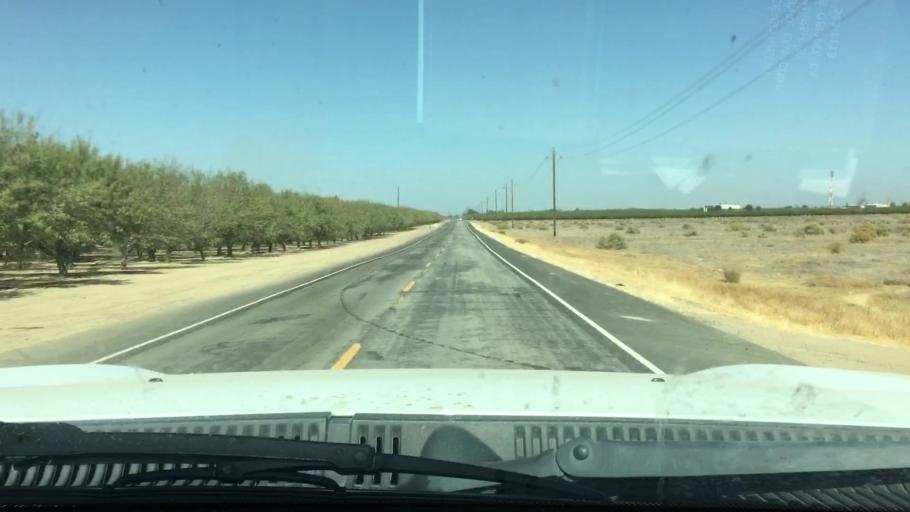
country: US
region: California
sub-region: Kern County
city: Shafter
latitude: 35.4485
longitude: -119.2789
